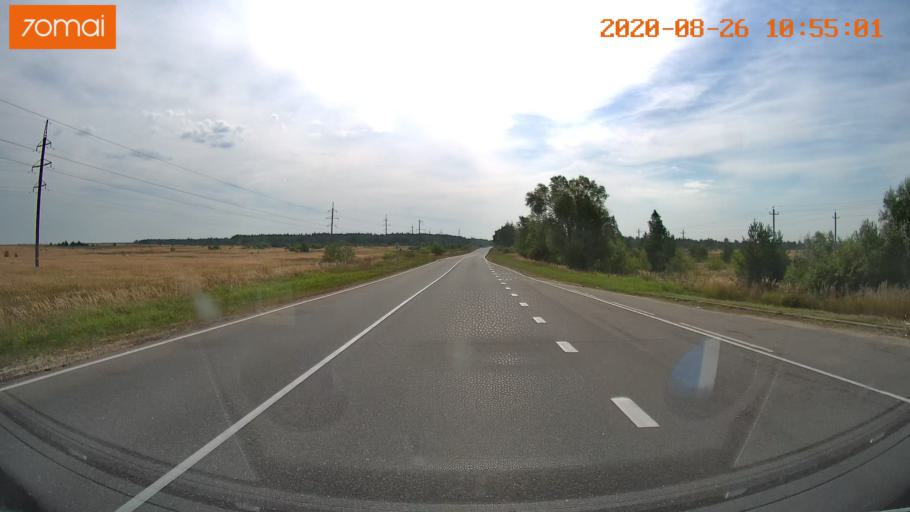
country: RU
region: Rjazan
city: Izhevskoye
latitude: 54.6217
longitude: 41.1720
